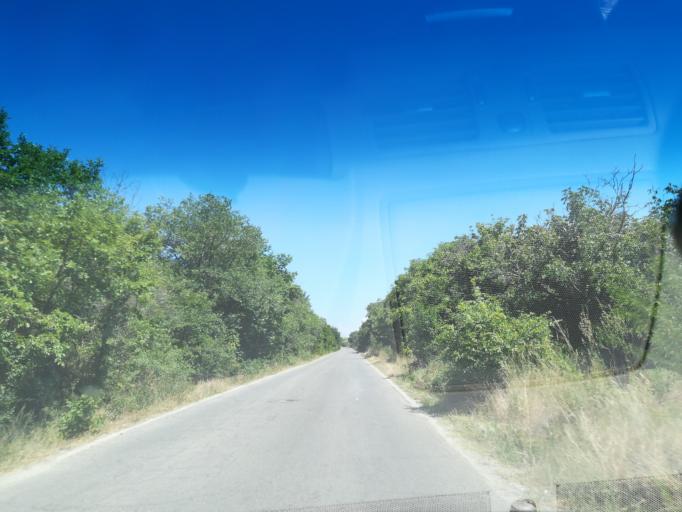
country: BG
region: Plovdiv
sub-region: Obshtina Sadovo
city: Sadovo
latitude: 42.0253
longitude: 24.9906
